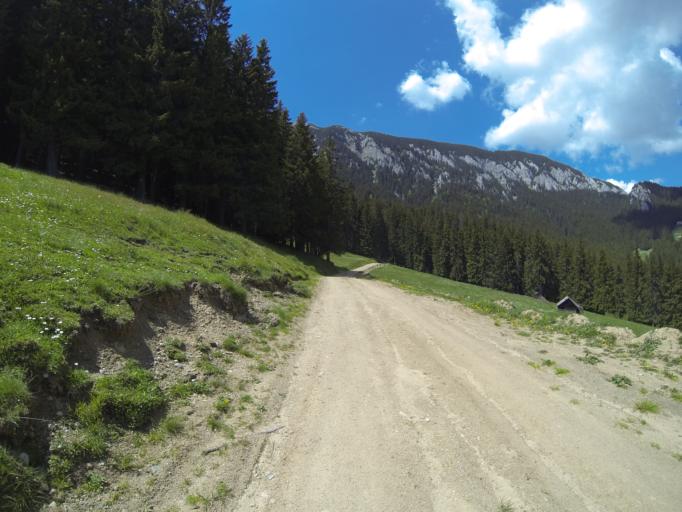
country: RO
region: Brasov
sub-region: Comuna Zarnesti
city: Zarnesti
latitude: 45.5447
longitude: 25.2517
